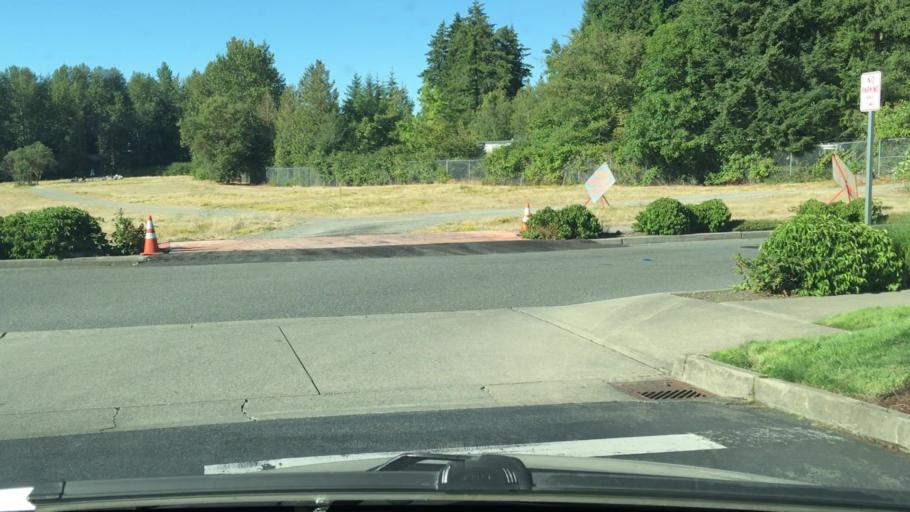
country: US
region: Washington
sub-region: King County
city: Eastgate
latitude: 47.5836
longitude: -122.1287
